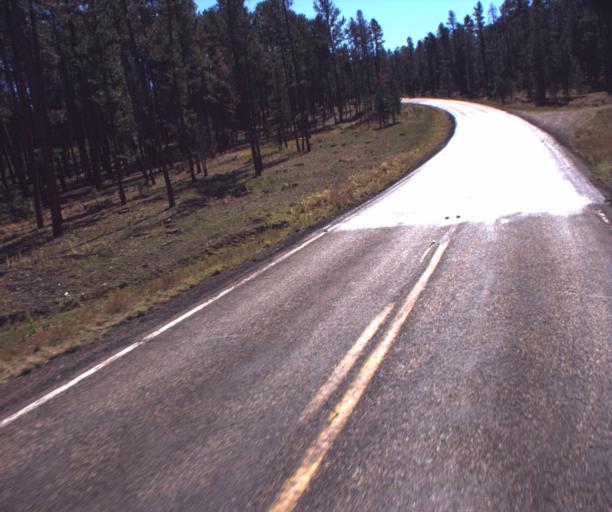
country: US
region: Arizona
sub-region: Coconino County
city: Fredonia
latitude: 36.7380
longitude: -112.2285
